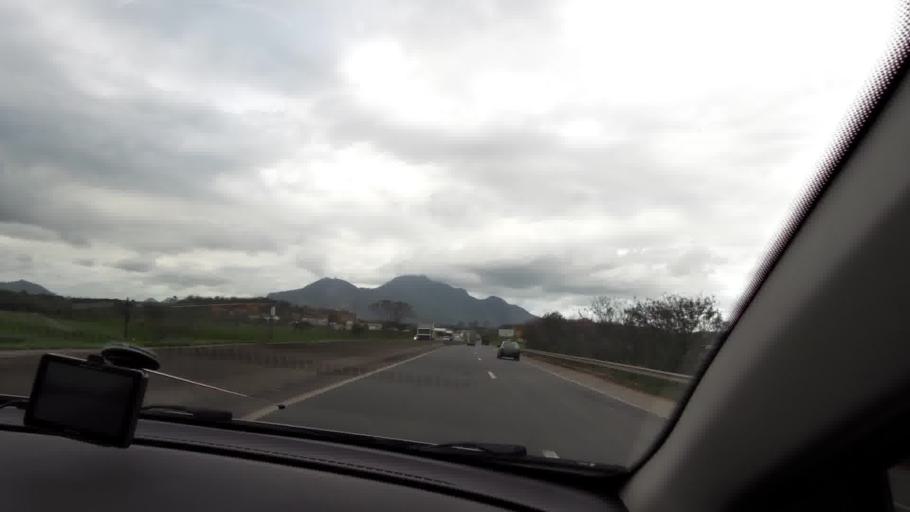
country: BR
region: Espirito Santo
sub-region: Vitoria
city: Vitoria
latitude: -20.2231
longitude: -40.3590
